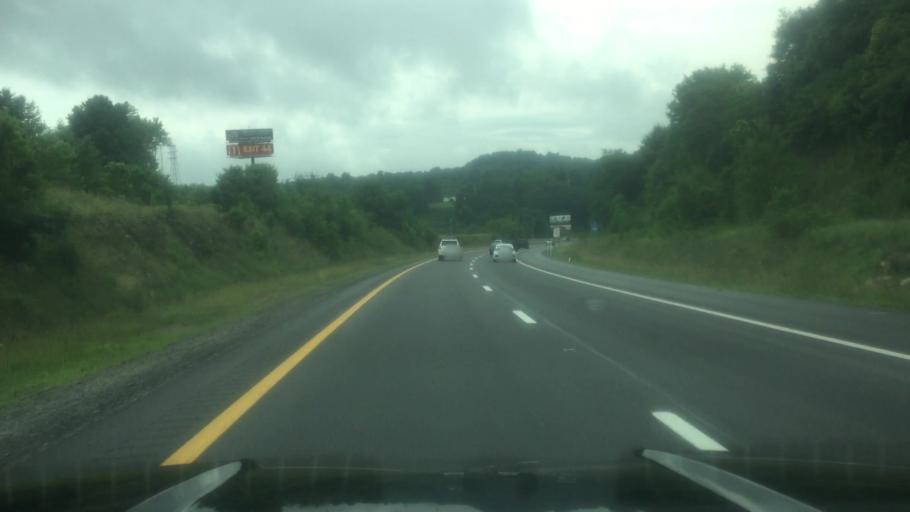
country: US
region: West Virginia
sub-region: Raleigh County
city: MacArthur
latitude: 37.7380
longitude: -81.2070
